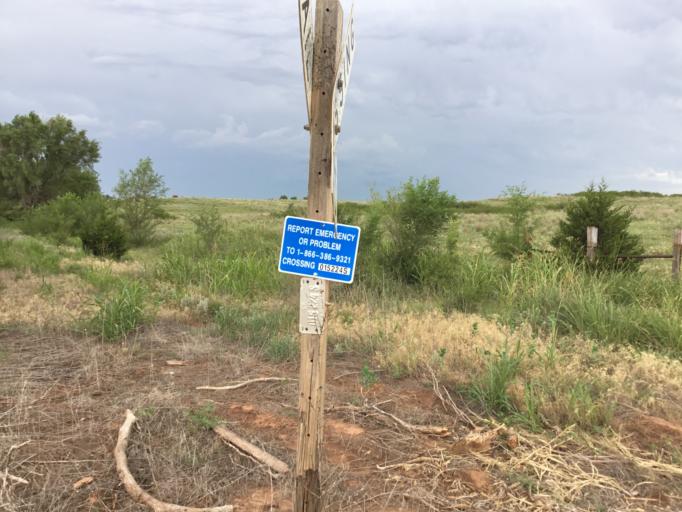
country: US
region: Kansas
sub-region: Kingman County
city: Kingman
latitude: 37.6327
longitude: -98.0272
